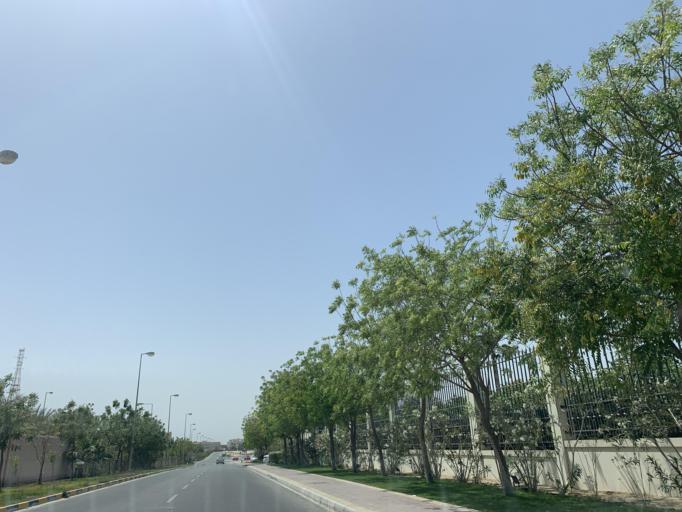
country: BH
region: Northern
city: Ar Rifa'
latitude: 26.1458
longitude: 50.5500
